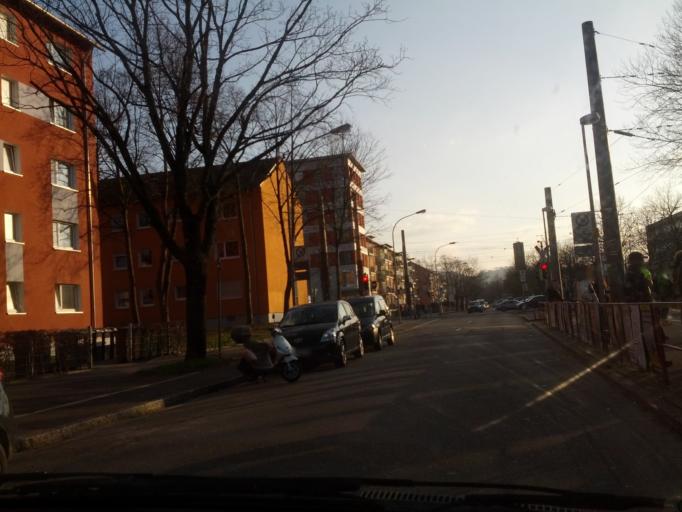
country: DE
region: Baden-Wuerttemberg
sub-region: Freiburg Region
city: Freiburg
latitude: 48.0004
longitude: 7.8331
